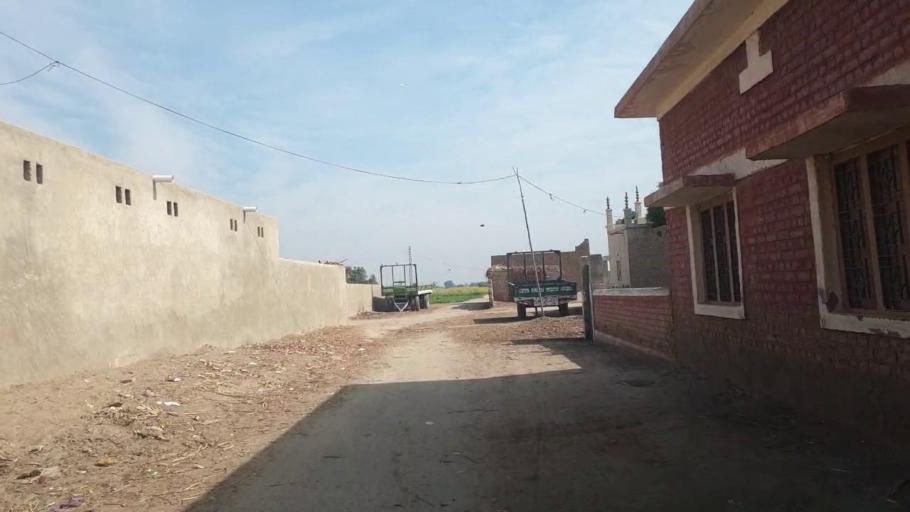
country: PK
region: Sindh
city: Shahpur Chakar
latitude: 26.1401
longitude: 68.5098
